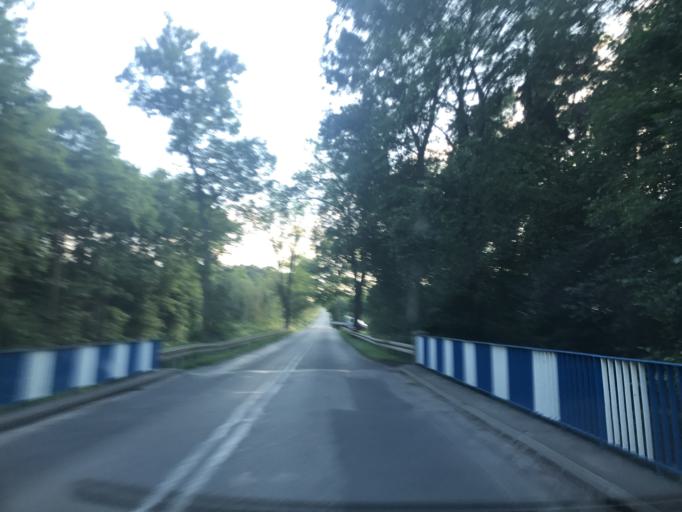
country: PL
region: Greater Poland Voivodeship
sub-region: Powiat jarocinski
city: Jarocin
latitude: 51.9861
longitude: 17.5443
